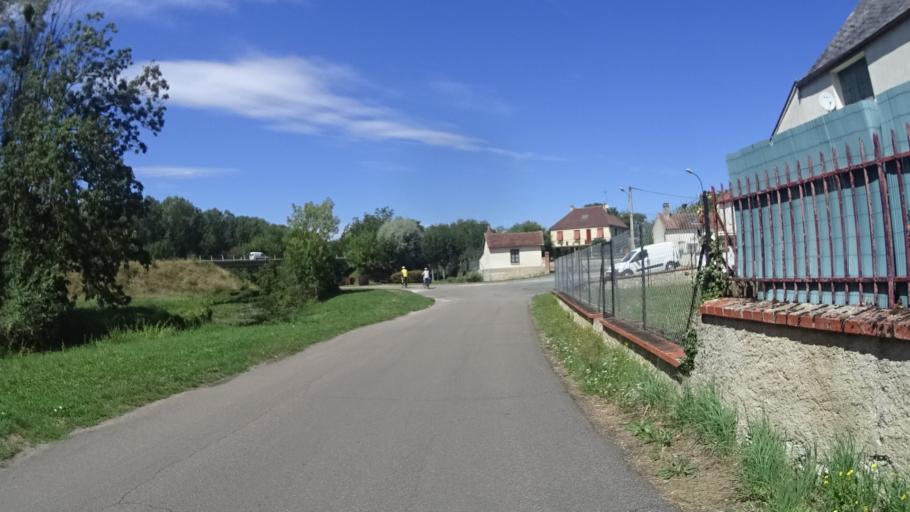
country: FR
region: Centre
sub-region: Departement du Loiret
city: Bonny-sur-Loire
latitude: 47.5629
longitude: 2.8349
